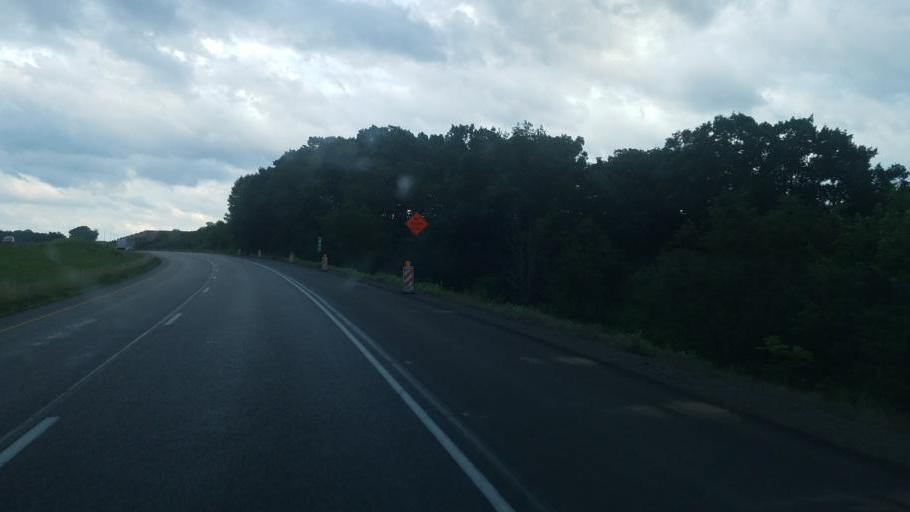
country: US
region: Pennsylvania
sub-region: Butler County
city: Zelienople
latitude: 40.7674
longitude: -80.1288
